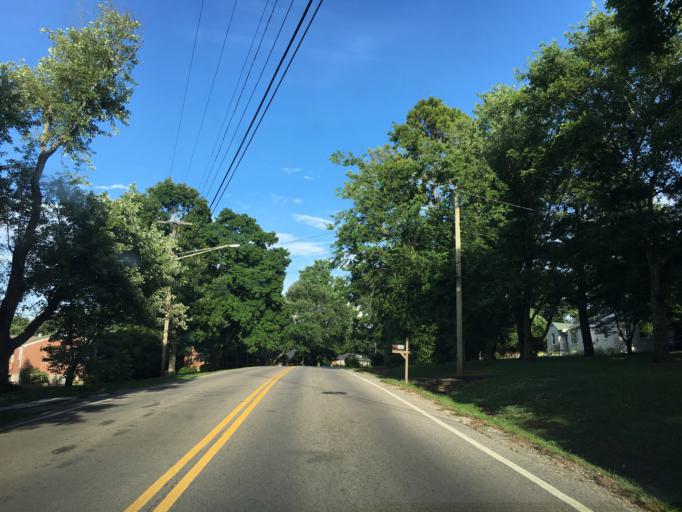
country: US
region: Tennessee
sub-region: Davidson County
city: Oak Hill
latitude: 36.0643
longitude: -86.7252
